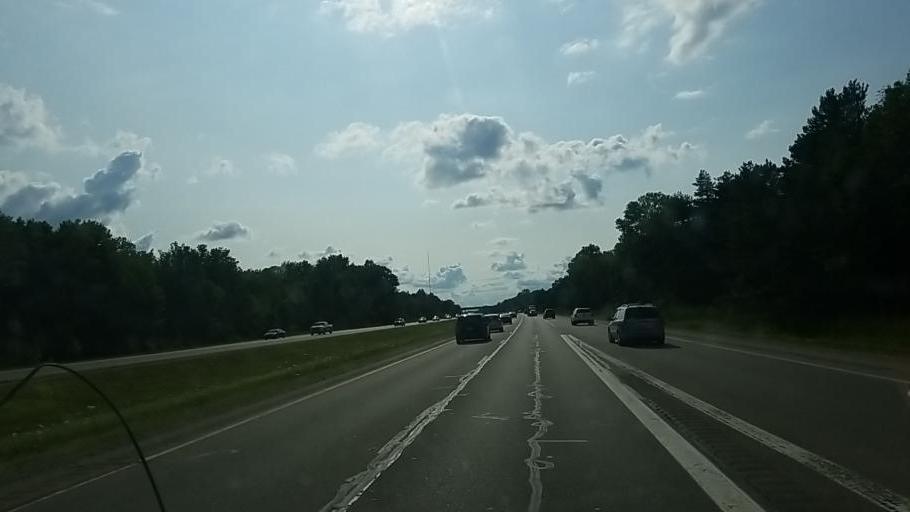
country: US
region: Michigan
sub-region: Eaton County
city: Dimondale
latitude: 42.6654
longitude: -84.5940
